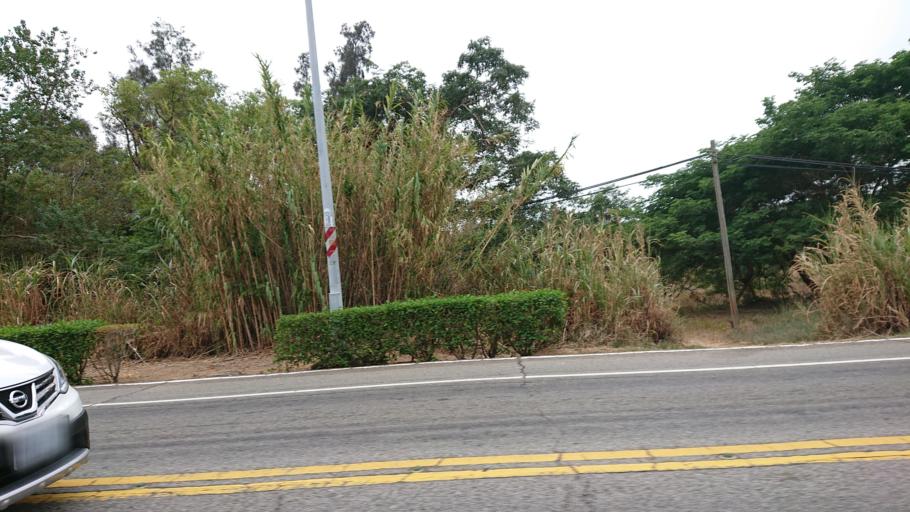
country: TW
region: Fukien
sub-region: Kinmen
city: Jincheng
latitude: 24.4458
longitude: 118.3867
